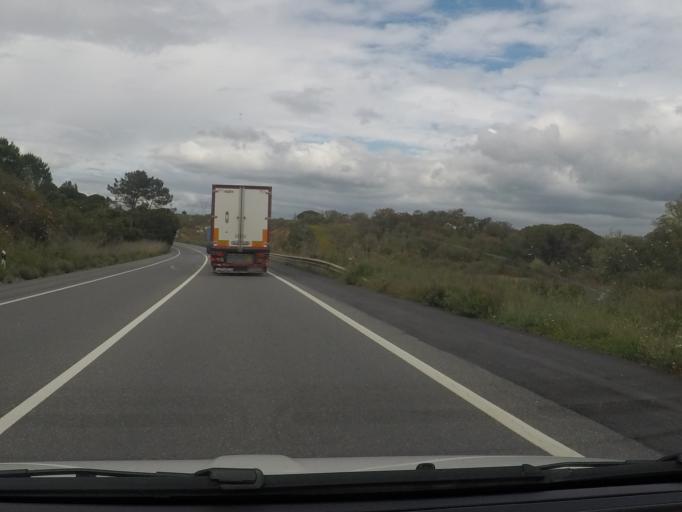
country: PT
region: Setubal
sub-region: Santiago do Cacem
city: Santiago do Cacem
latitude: 38.0760
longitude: -8.6447
